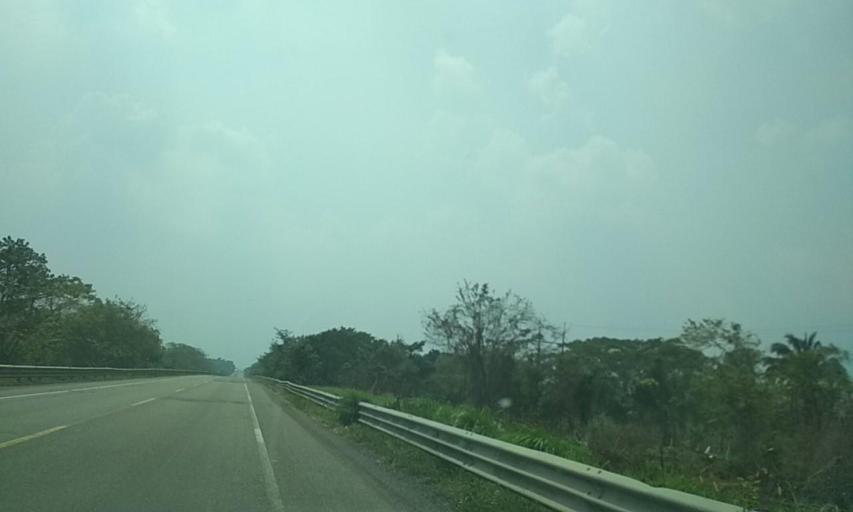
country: MX
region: Tabasco
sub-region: Huimanguillo
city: Francisco Rueda
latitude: 17.7628
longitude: -94.0146
